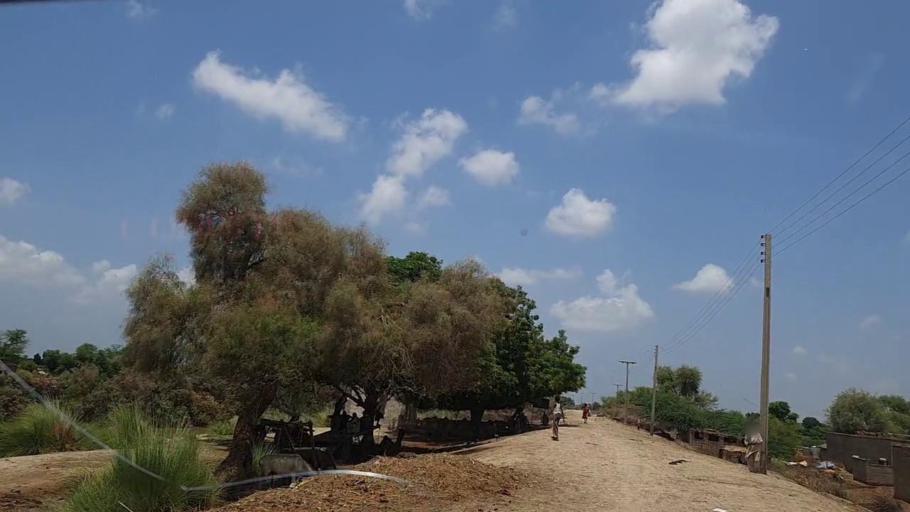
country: PK
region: Sindh
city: Tharu Shah
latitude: 26.9226
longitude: 67.9897
